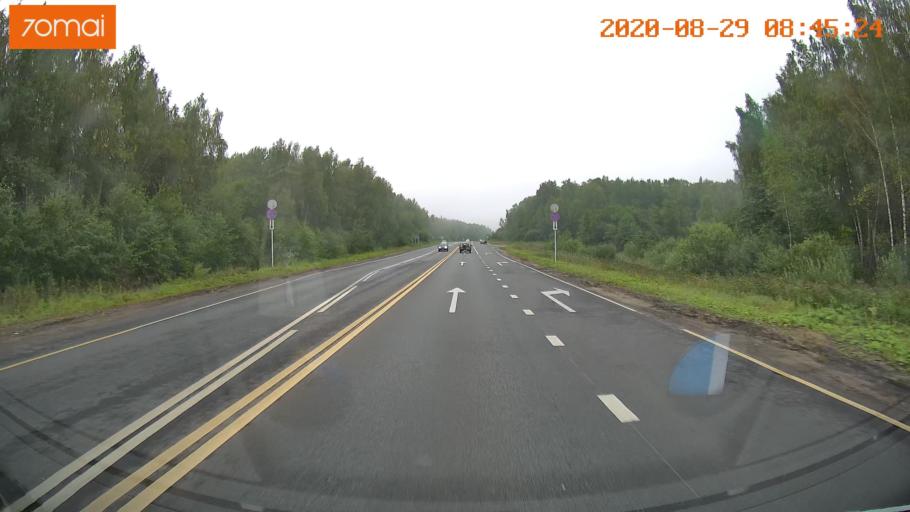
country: RU
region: Ivanovo
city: Rodniki
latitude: 57.1302
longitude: 41.8003
